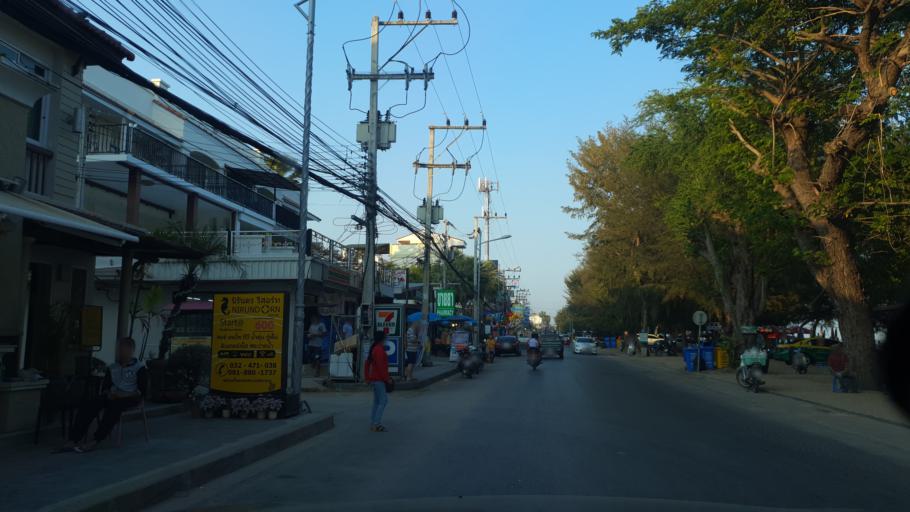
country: TH
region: Phetchaburi
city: Cha-am
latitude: 12.7954
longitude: 99.9841
